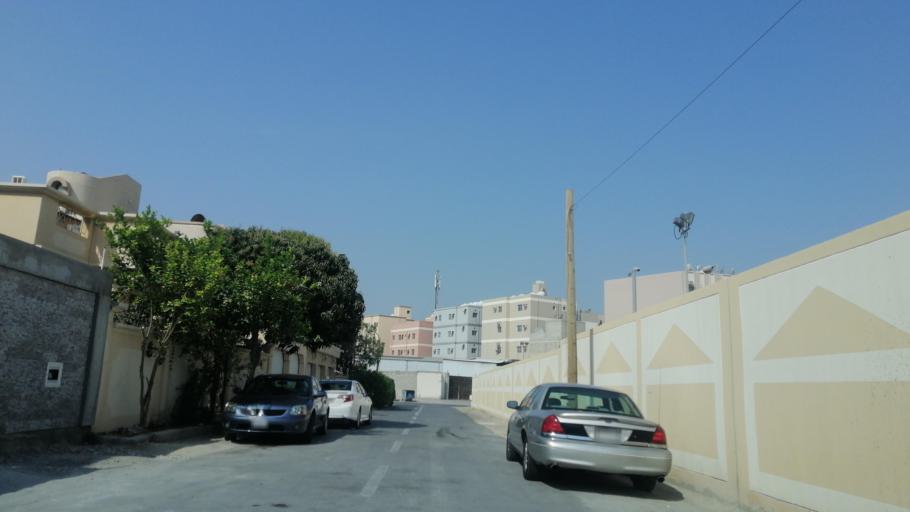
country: BH
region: Muharraq
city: Al Hadd
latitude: 26.2555
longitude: 50.6371
